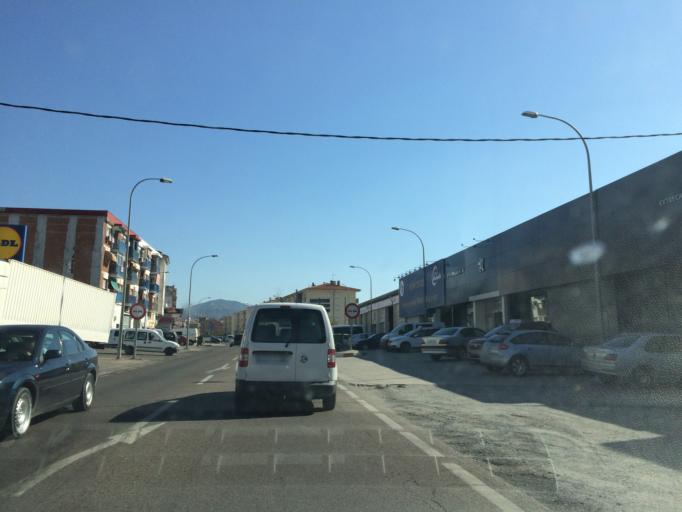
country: ES
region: Extremadura
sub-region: Provincia de Caceres
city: Plasencia
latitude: 40.0216
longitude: -6.0979
